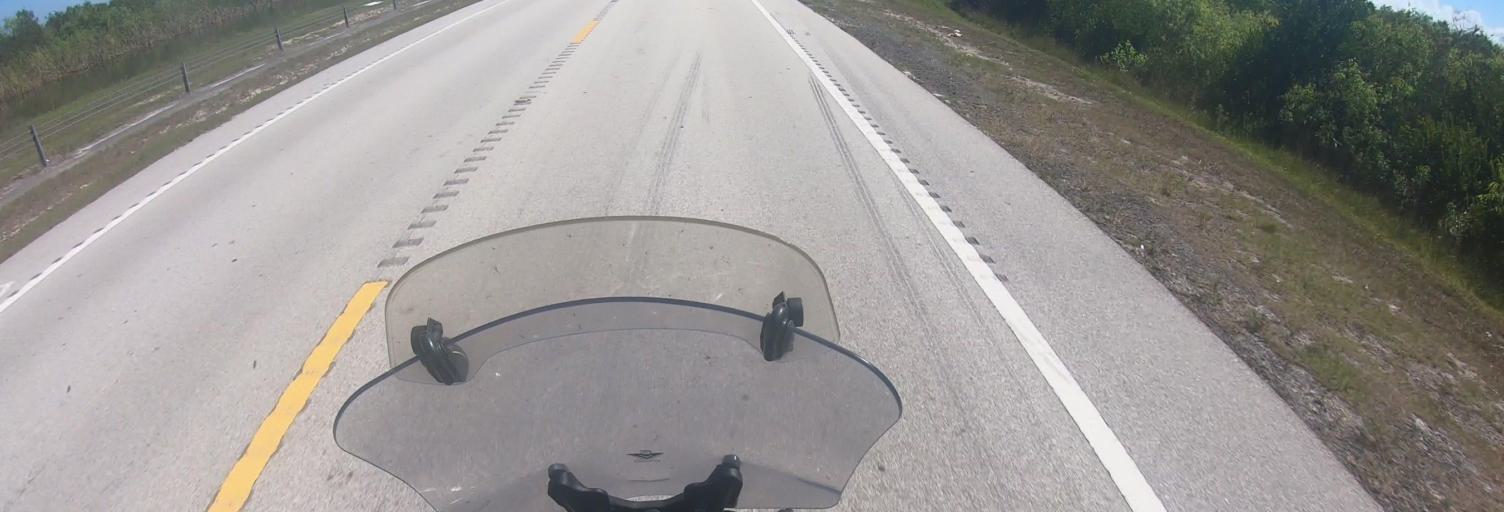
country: US
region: Florida
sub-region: Miami-Dade County
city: Kendall West
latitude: 25.7610
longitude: -80.7511
